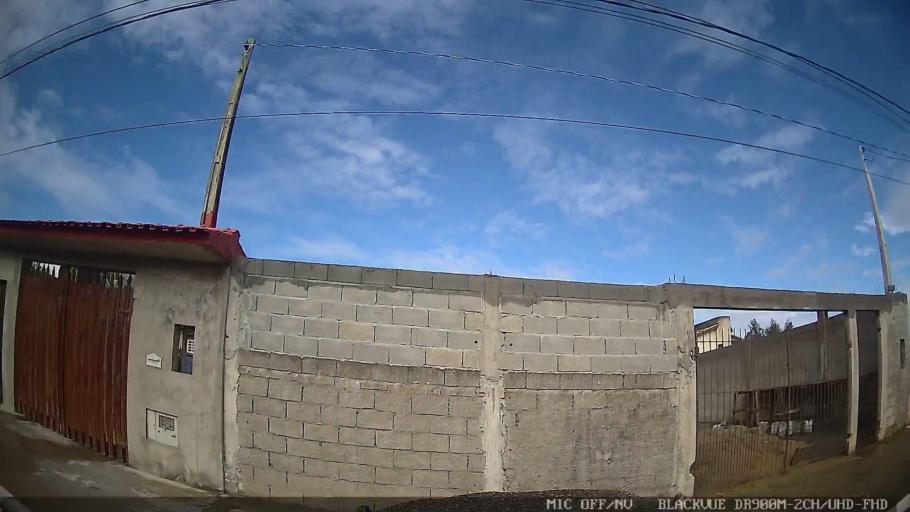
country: BR
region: Sao Paulo
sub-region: Itanhaem
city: Itanhaem
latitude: -24.2338
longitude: -46.8818
